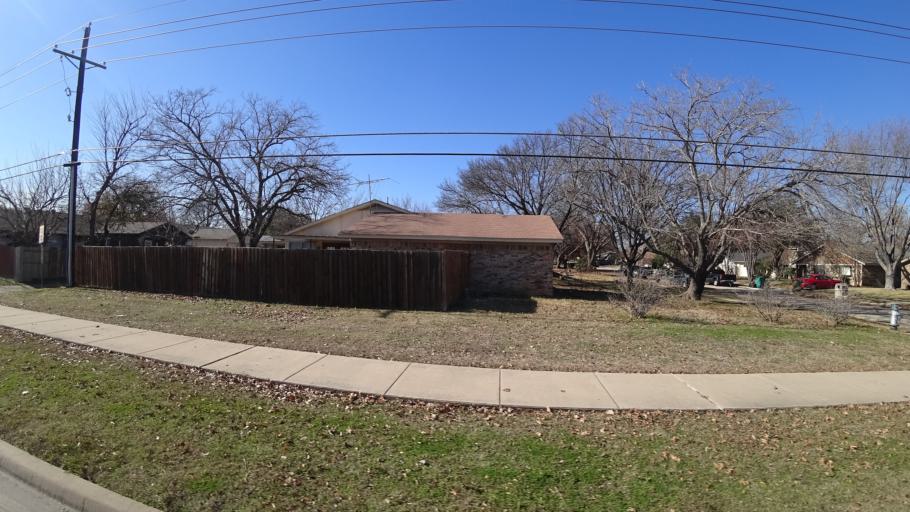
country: US
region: Texas
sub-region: Denton County
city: Lewisville
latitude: 33.0298
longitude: -97.0105
